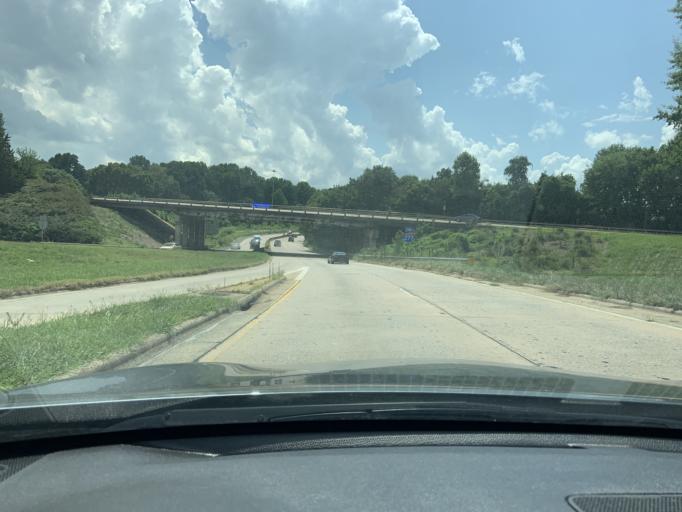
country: US
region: North Carolina
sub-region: Mecklenburg County
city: Charlotte
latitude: 35.2247
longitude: -80.8674
